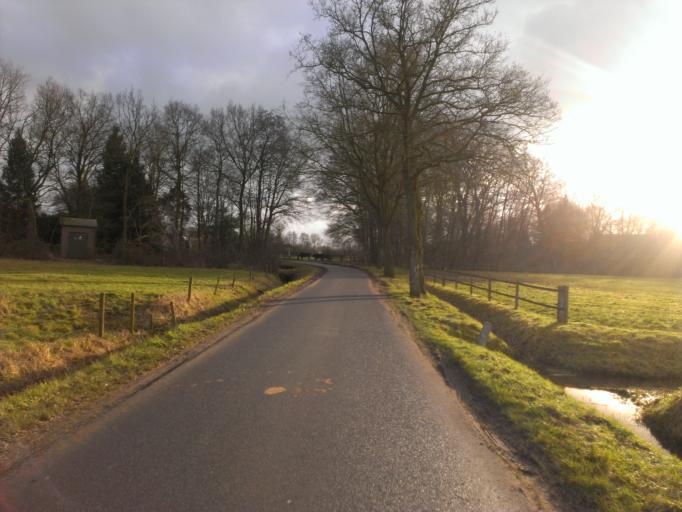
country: NL
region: Gelderland
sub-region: Gemeente Heerde
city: Heerde
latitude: 52.3719
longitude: 6.0291
